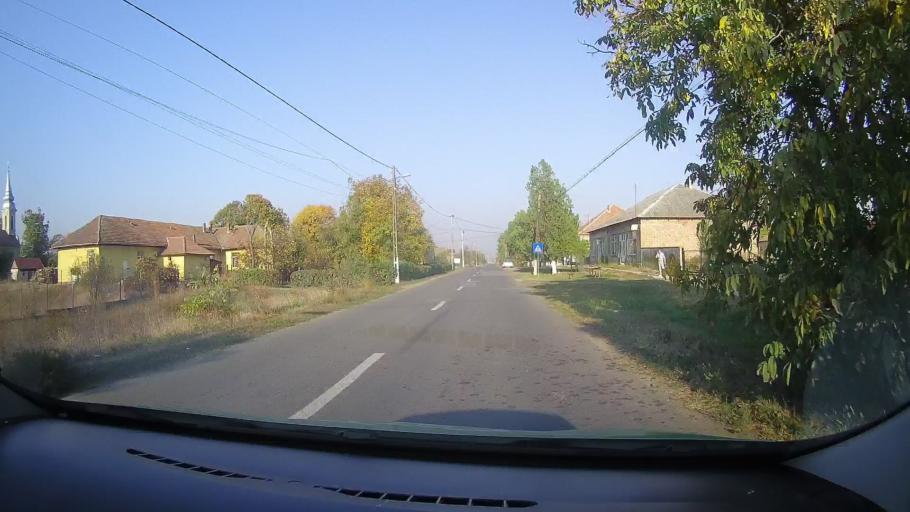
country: RO
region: Arad
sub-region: Comuna Graniceri
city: Siclau
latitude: 46.4932
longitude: 21.3666
